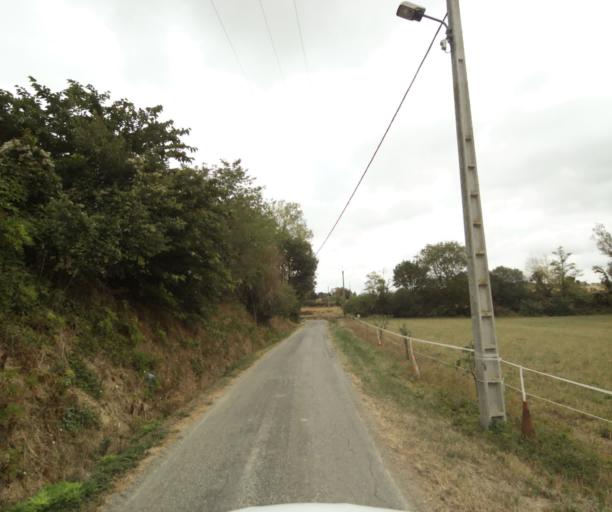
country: FR
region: Midi-Pyrenees
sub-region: Departement de la Haute-Garonne
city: Villefranche-de-Lauragais
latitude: 43.4114
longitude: 1.7177
